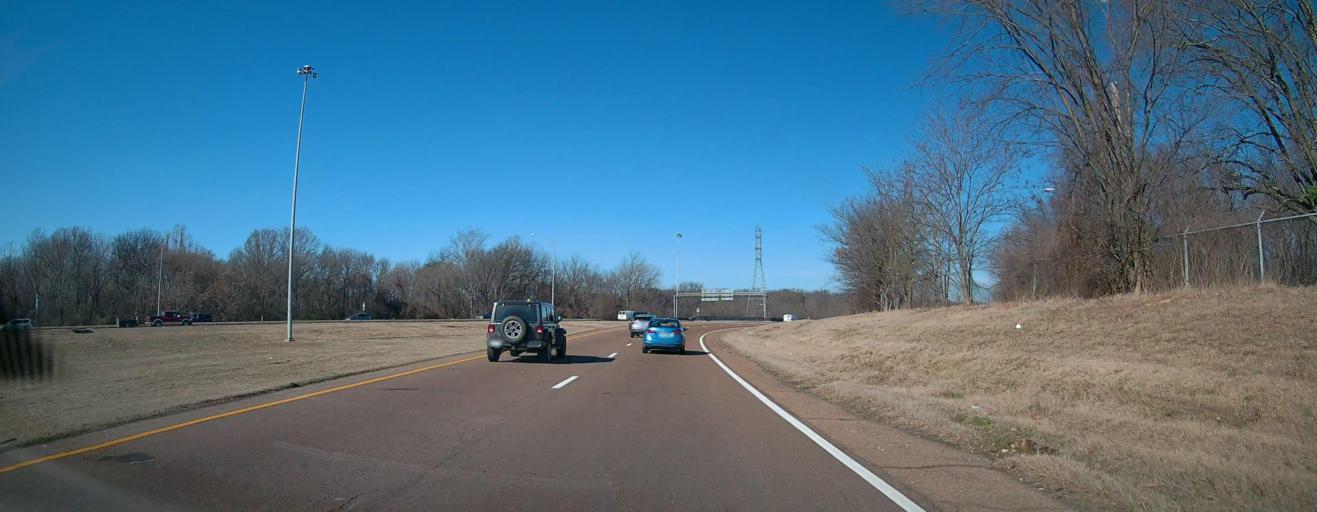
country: US
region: Tennessee
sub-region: Shelby County
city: Bartlett
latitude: 35.1941
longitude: -89.9246
